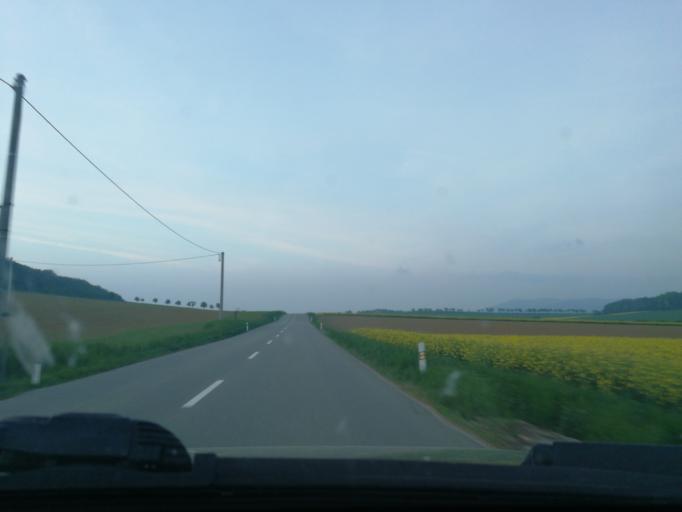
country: CZ
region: Zlin
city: Holesov
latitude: 49.2809
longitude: 17.5503
